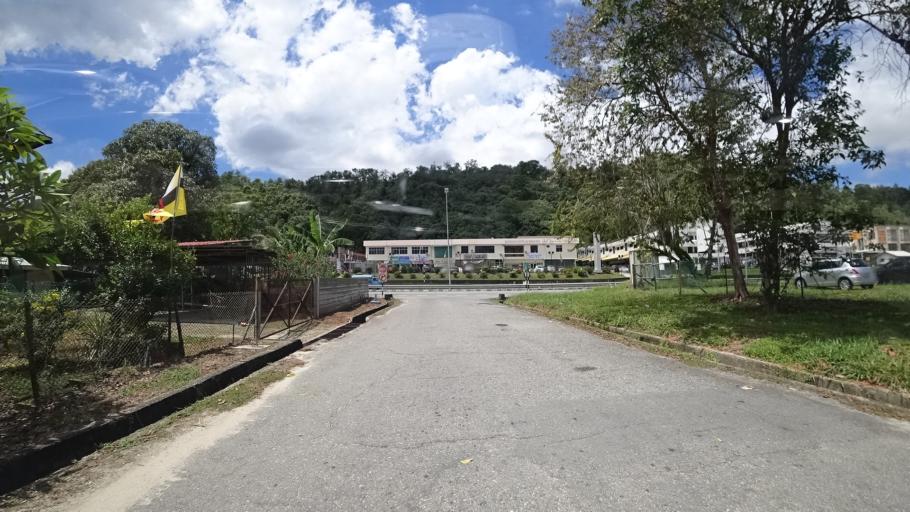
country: BN
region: Brunei and Muara
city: Bandar Seri Begawan
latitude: 4.8561
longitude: 114.8921
